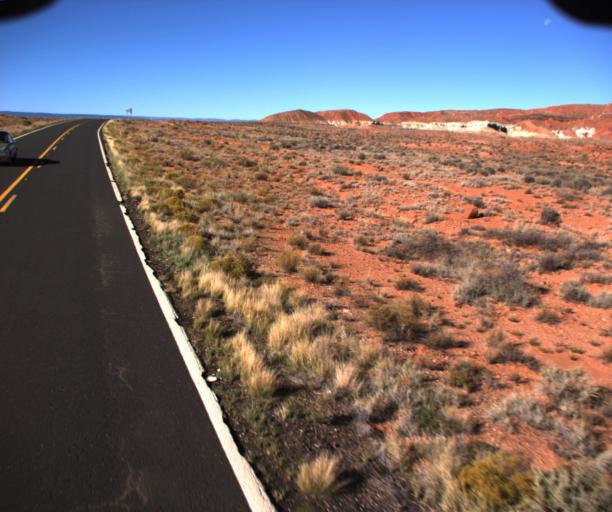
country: US
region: Arizona
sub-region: Coconino County
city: LeChee
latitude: 36.6890
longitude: -111.8218
